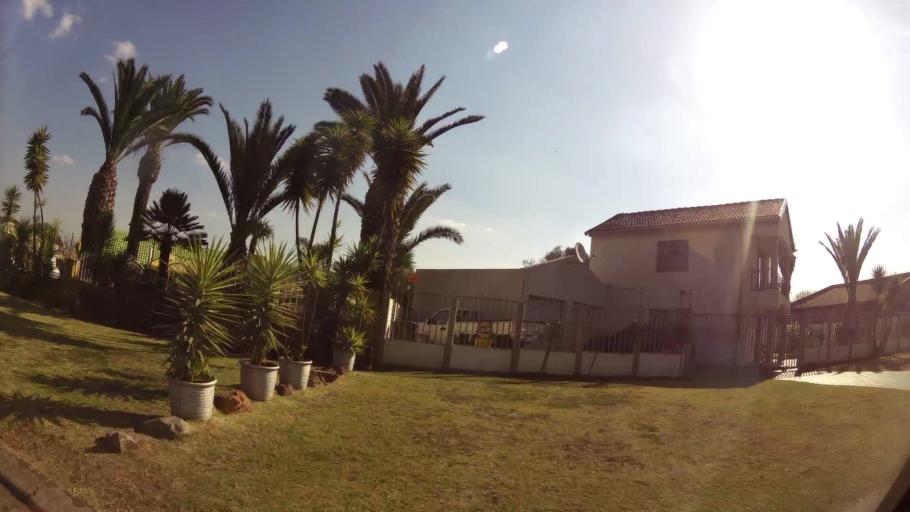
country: ZA
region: Gauteng
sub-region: Ekurhuleni Metropolitan Municipality
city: Benoni
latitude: -26.2425
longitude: 28.3140
